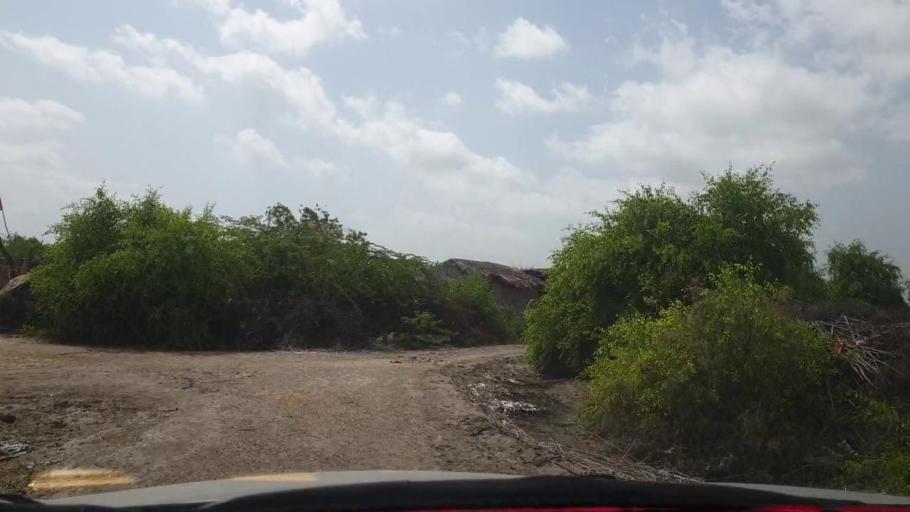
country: PK
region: Sindh
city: Rajo Khanani
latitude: 24.9111
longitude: 68.9211
